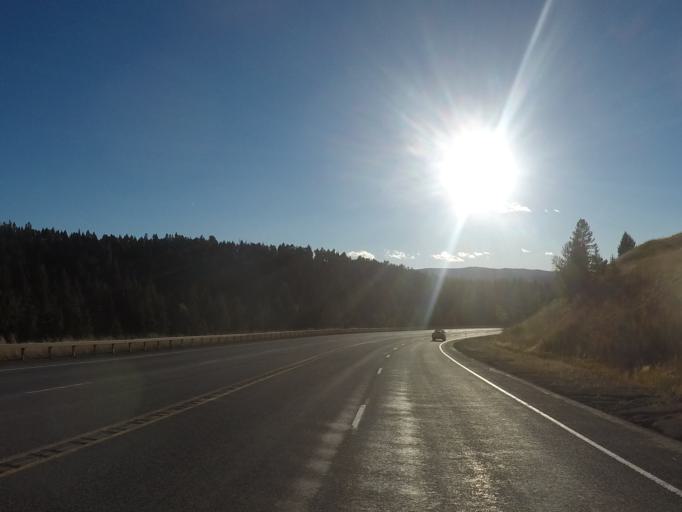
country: US
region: Montana
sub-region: Lewis and Clark County
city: Helena West Side
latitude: 46.5570
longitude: -112.3604
